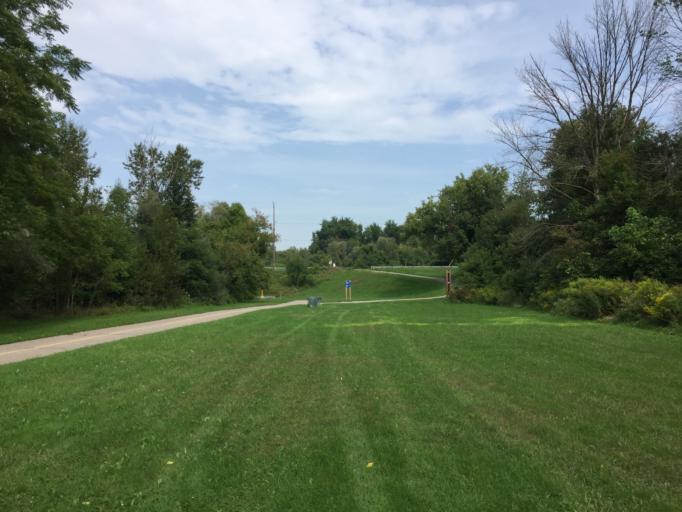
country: CA
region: Ontario
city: Oshawa
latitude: 43.9093
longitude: -78.8422
